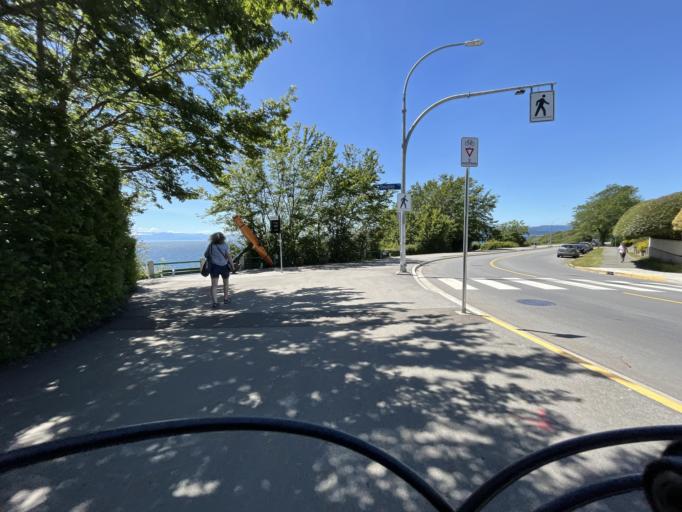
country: CA
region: British Columbia
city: Victoria
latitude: 48.4087
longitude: -123.3694
